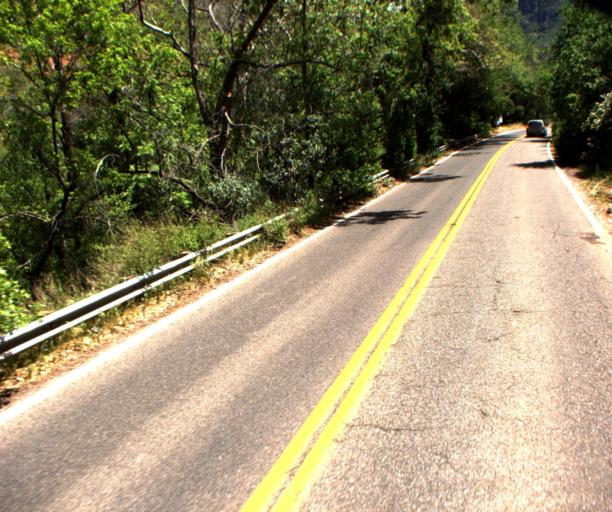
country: US
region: Arizona
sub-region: Coconino County
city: Sedona
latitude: 34.9197
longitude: -111.7328
